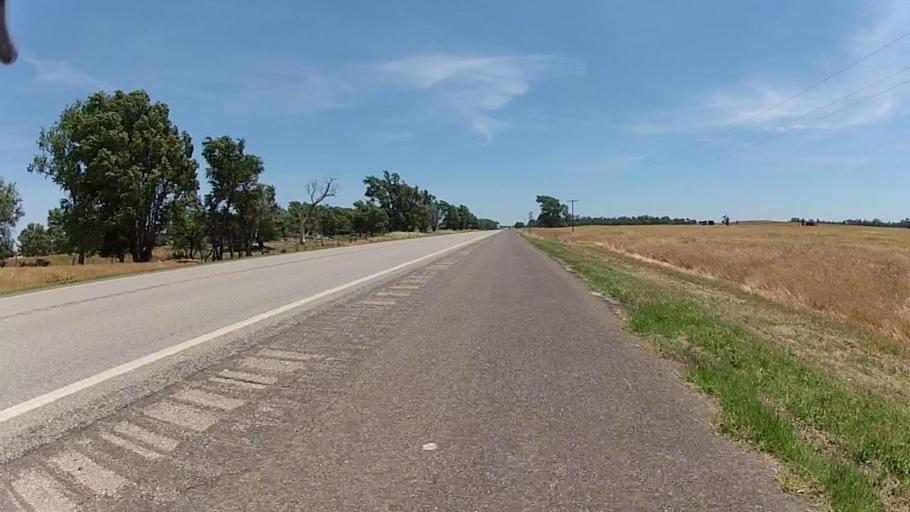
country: US
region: Kansas
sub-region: Barber County
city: Medicine Lodge
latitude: 37.2536
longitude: -98.3795
